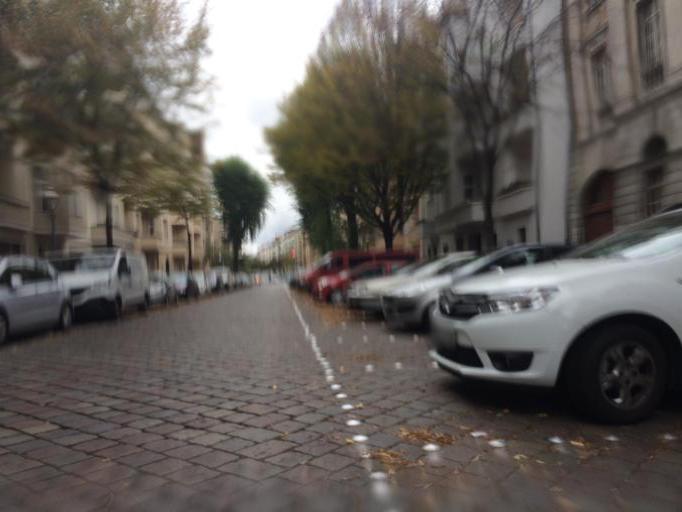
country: DE
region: Berlin
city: Wedding Bezirk
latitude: 52.5467
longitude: 13.3479
